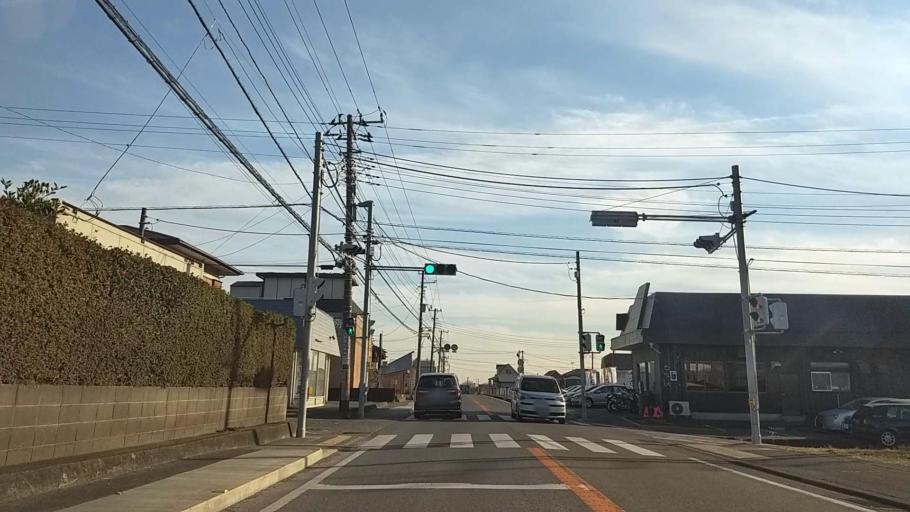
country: JP
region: Kanagawa
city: Zama
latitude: 35.5048
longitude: 139.3098
